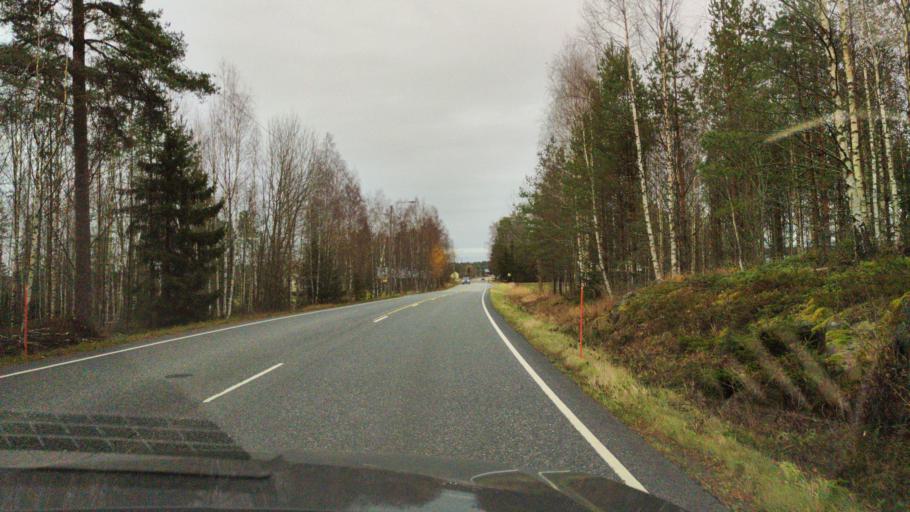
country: FI
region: Varsinais-Suomi
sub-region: Turku
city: Vahto
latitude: 60.6413
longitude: 22.4201
